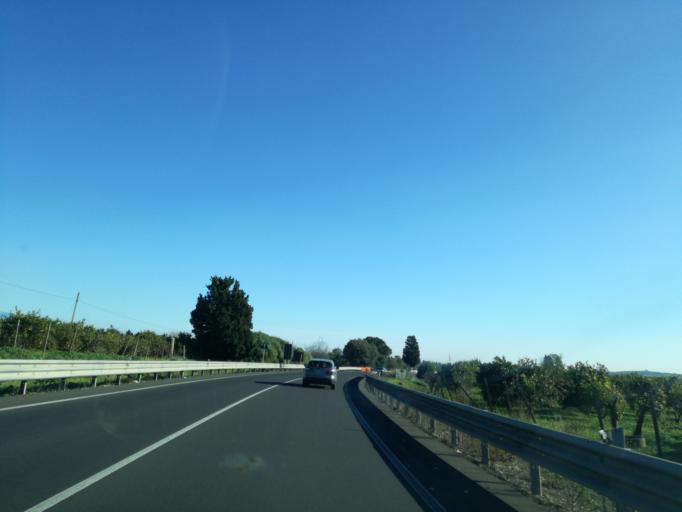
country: IT
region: Sicily
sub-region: Catania
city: Ramacca
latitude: 37.3759
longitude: 14.7296
